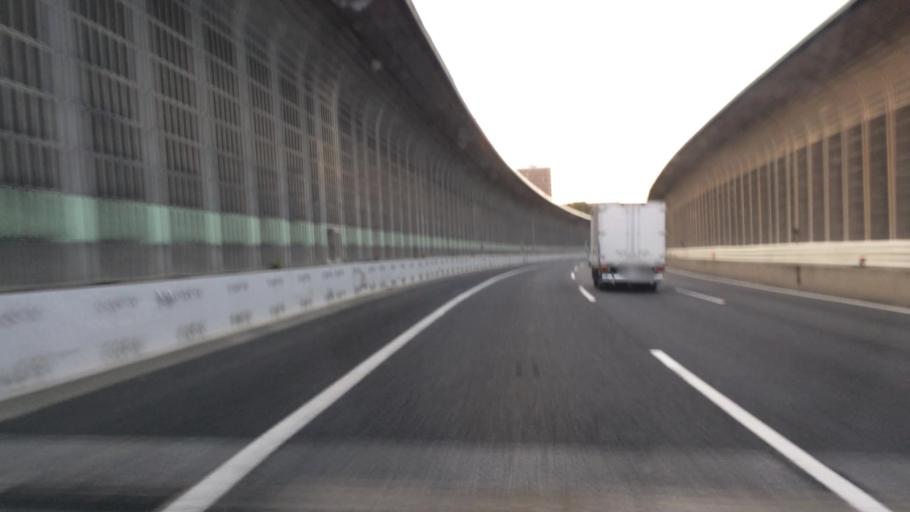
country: JP
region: Chiba
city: Chiba
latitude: 35.6428
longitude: 140.0705
